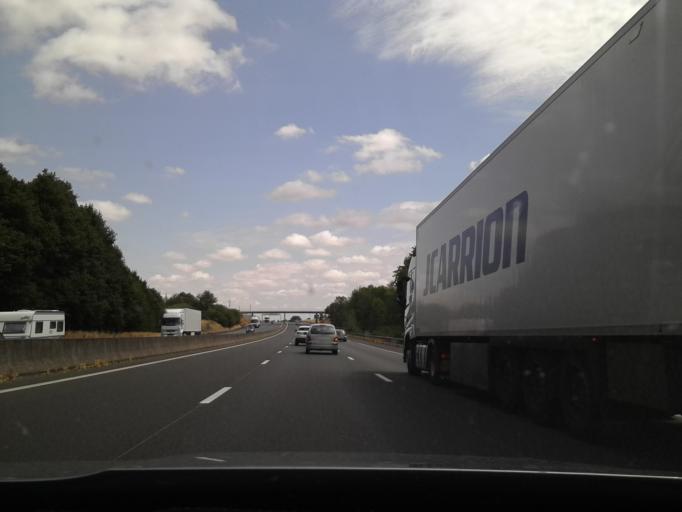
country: FR
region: Centre
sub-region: Departement d'Indre-et-Loire
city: Reugny
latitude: 47.4959
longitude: 0.8412
